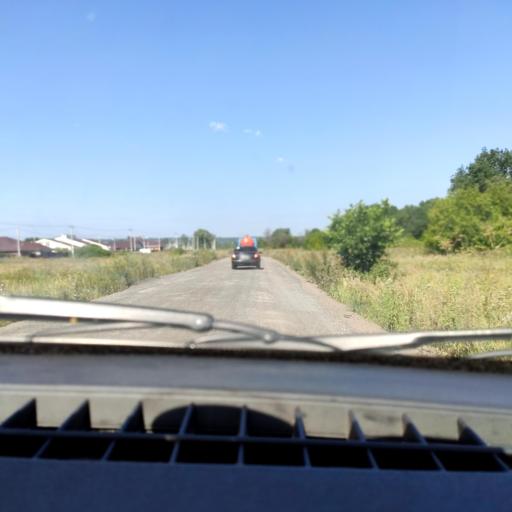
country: RU
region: Bashkortostan
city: Mikhaylovka
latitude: 54.8110
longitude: 55.9476
